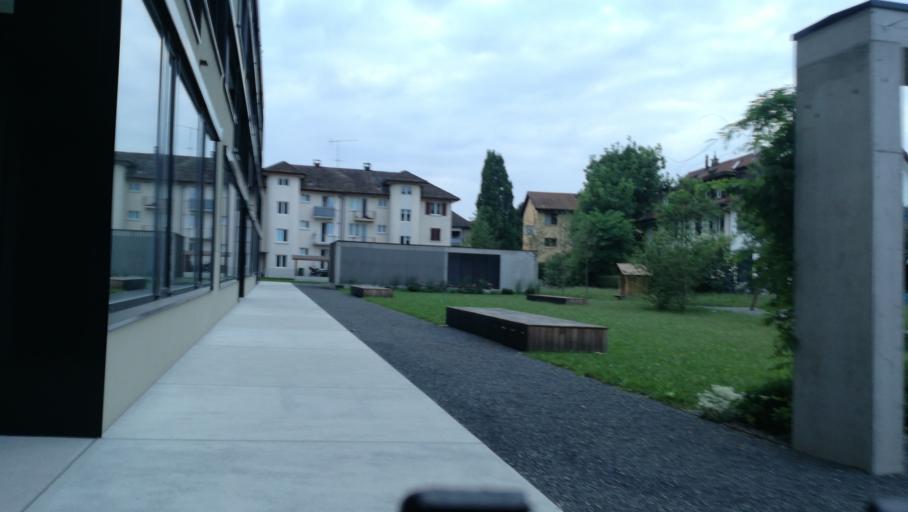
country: CH
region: Zug
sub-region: Zug
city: Zug
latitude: 47.1780
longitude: 8.5125
